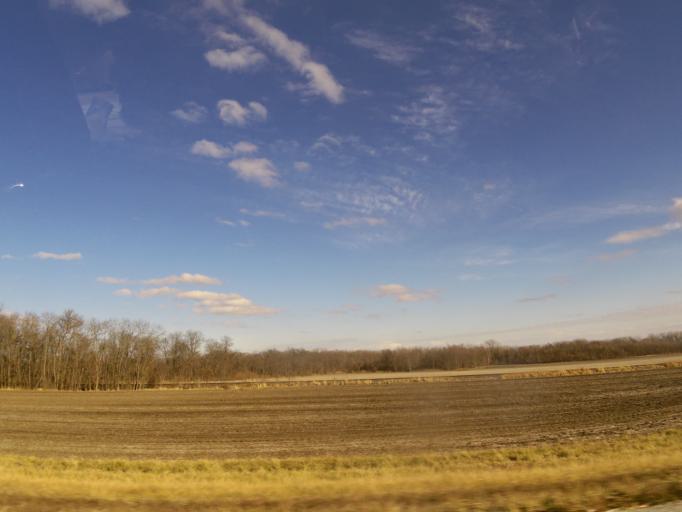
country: US
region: Missouri
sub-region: Lewis County
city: Canton
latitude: 40.1981
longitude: -91.5219
